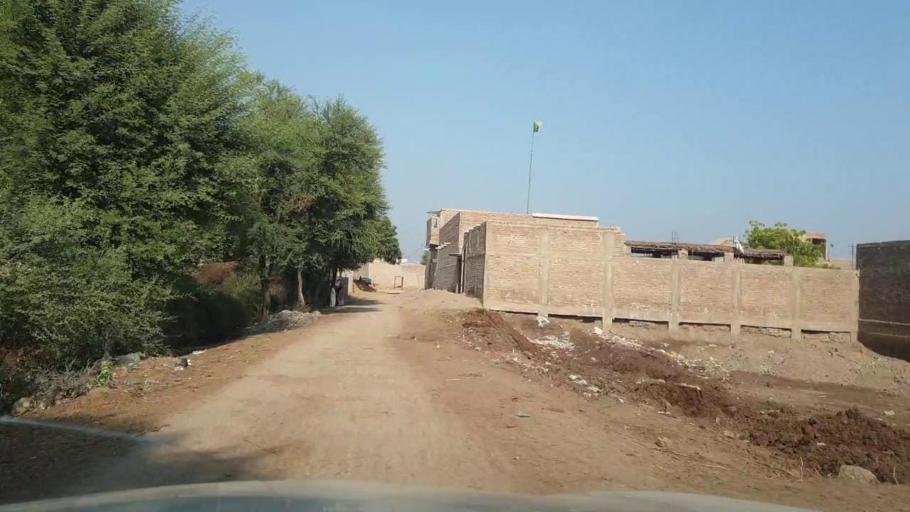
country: PK
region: Sindh
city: Bhan
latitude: 26.5466
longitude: 67.7440
